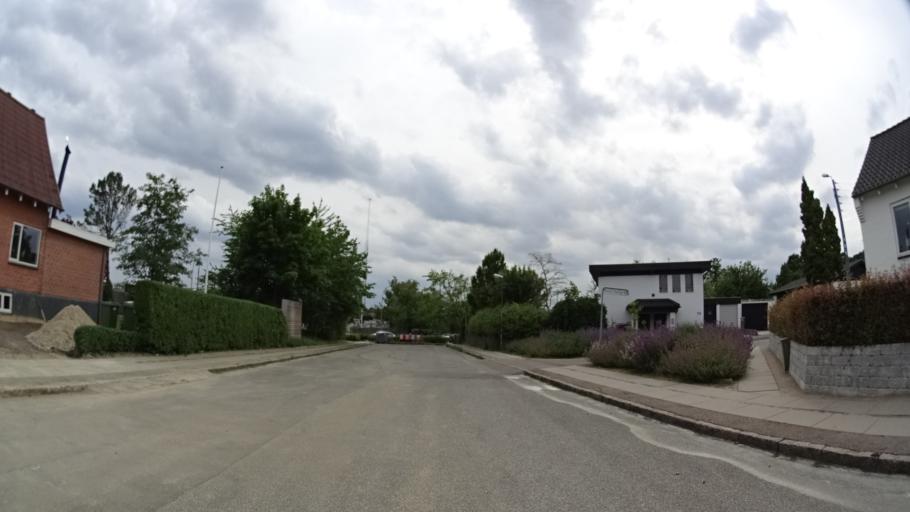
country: DK
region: Central Jutland
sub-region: Arhus Kommune
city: Stavtrup
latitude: 56.1473
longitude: 10.1532
